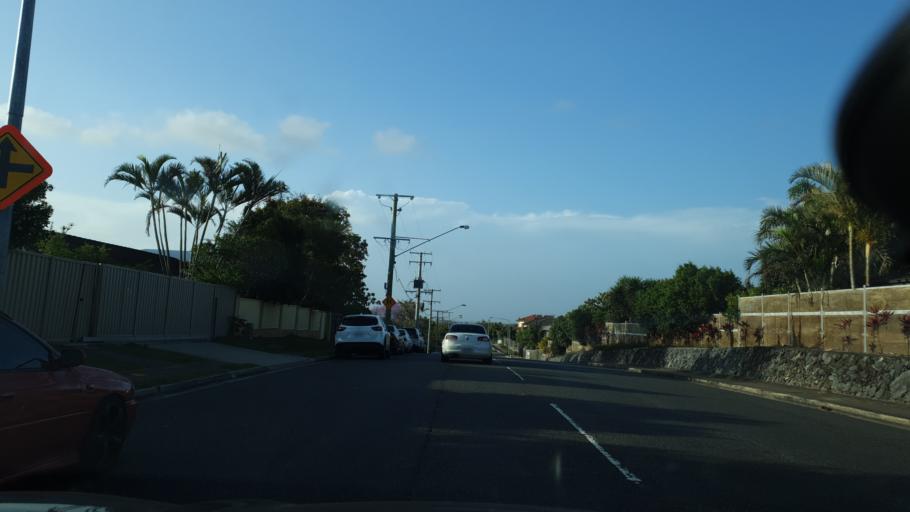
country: AU
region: Queensland
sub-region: Brisbane
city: Belmont
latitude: -27.4905
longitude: 153.1276
